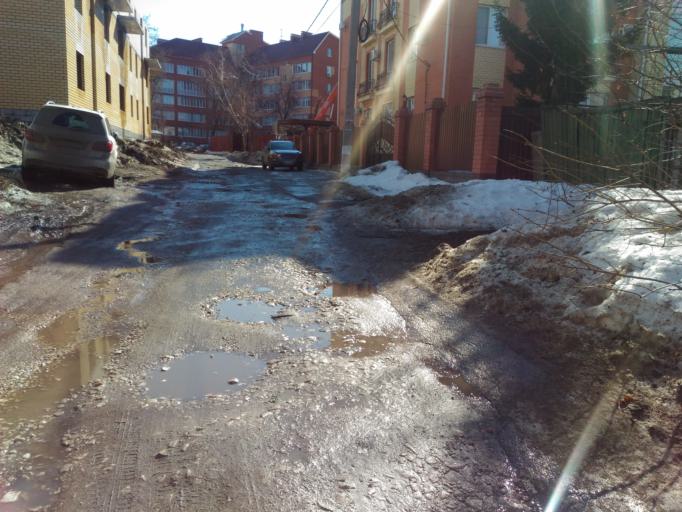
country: RU
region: Ulyanovsk
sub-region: Ulyanovskiy Rayon
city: Ulyanovsk
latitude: 54.3326
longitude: 48.3963
